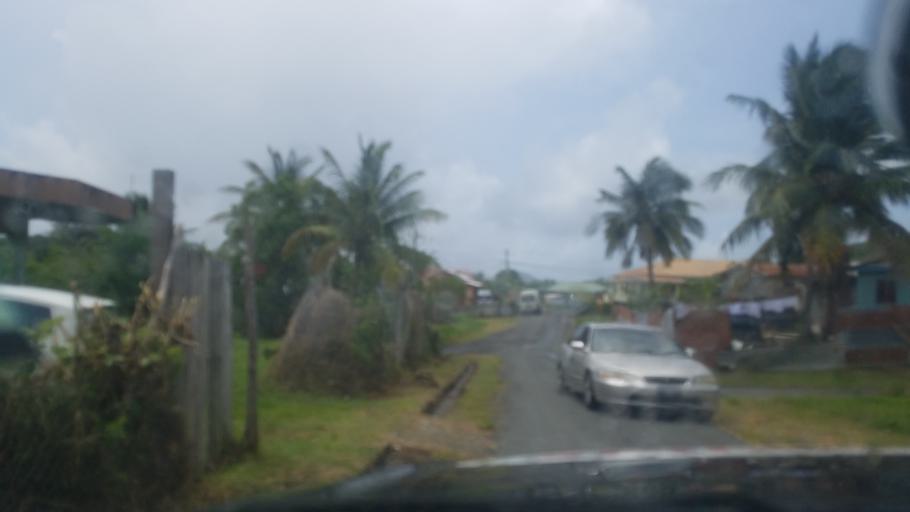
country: LC
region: Laborie Quarter
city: Laborie
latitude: 13.7471
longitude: -60.9645
